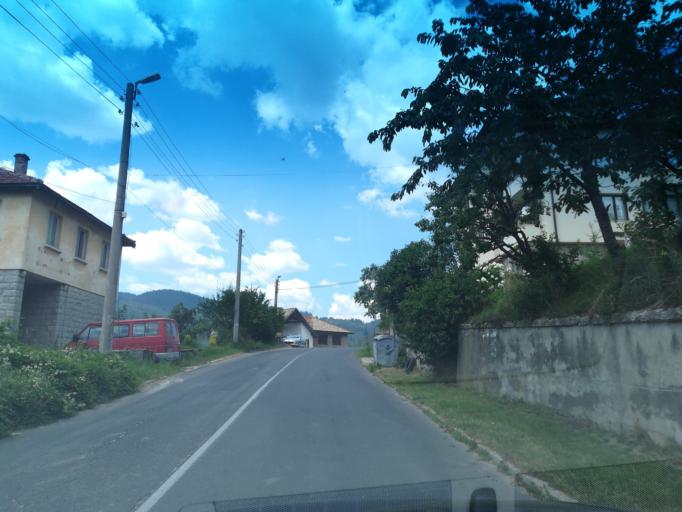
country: BG
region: Smolyan
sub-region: Obshtina Smolyan
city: Smolyan
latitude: 41.6563
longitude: 24.7684
